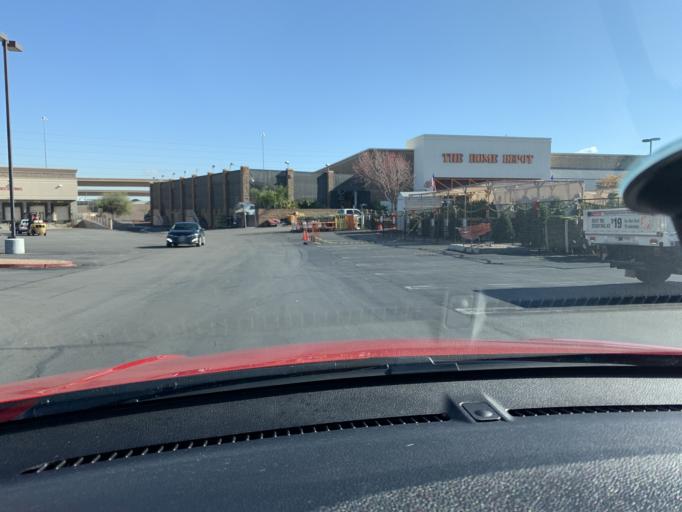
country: US
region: Nevada
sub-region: Clark County
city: Whitney
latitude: 36.0655
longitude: -115.0358
